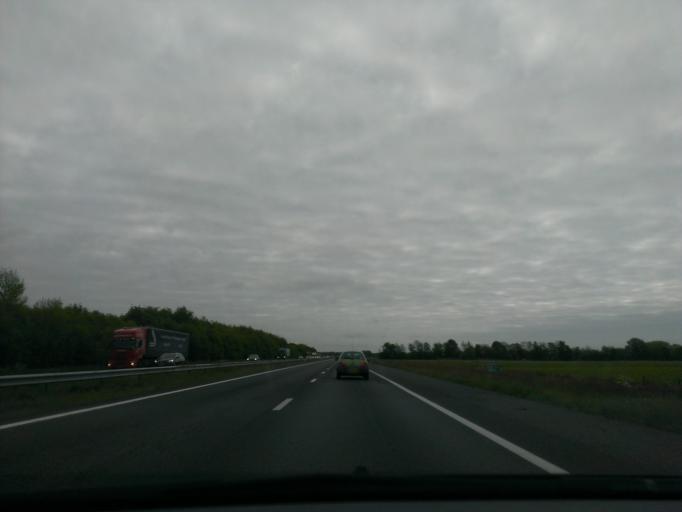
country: NL
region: Drenthe
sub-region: Gemeente De Wolden
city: Ruinen
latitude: 52.6790
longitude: 6.3050
